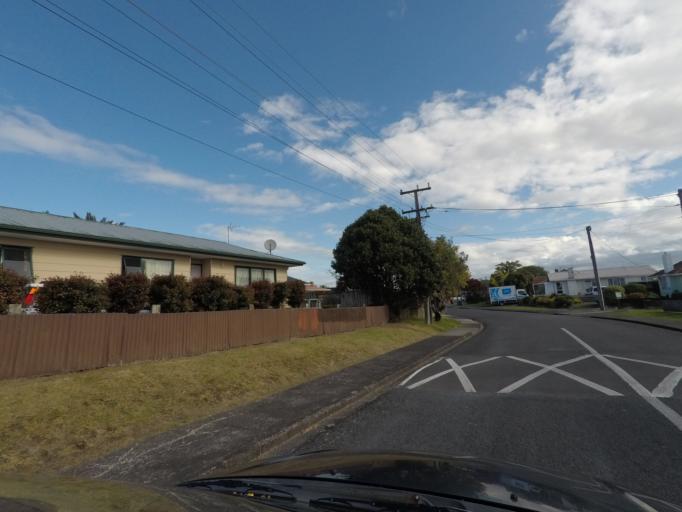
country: NZ
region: Auckland
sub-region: Auckland
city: Rosebank
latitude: -36.8694
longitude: 174.6425
